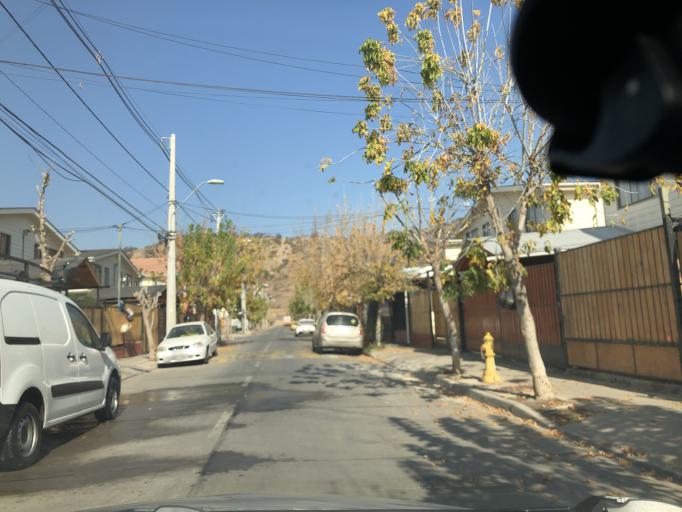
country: CL
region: Santiago Metropolitan
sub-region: Provincia de Cordillera
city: Puente Alto
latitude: -33.5983
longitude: -70.5511
